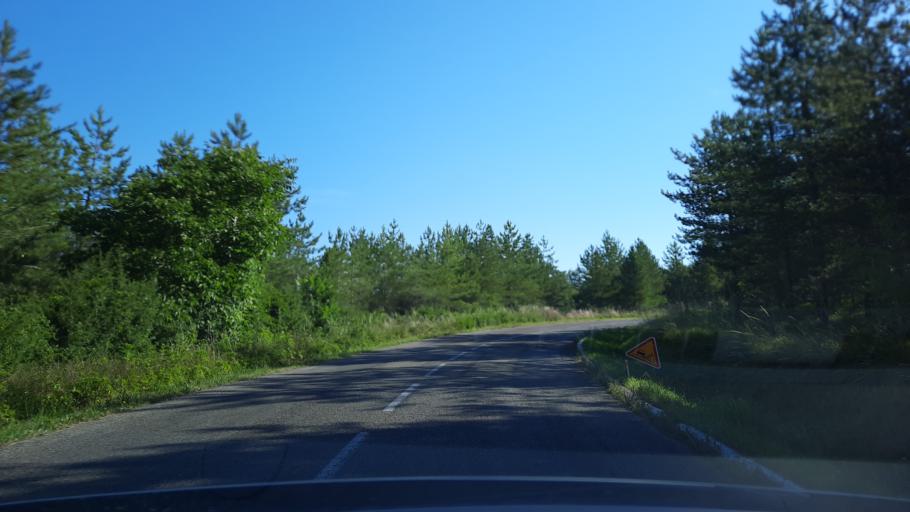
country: FR
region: Midi-Pyrenees
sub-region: Departement du Tarn-et-Garonne
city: Molieres
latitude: 44.1852
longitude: 1.3434
